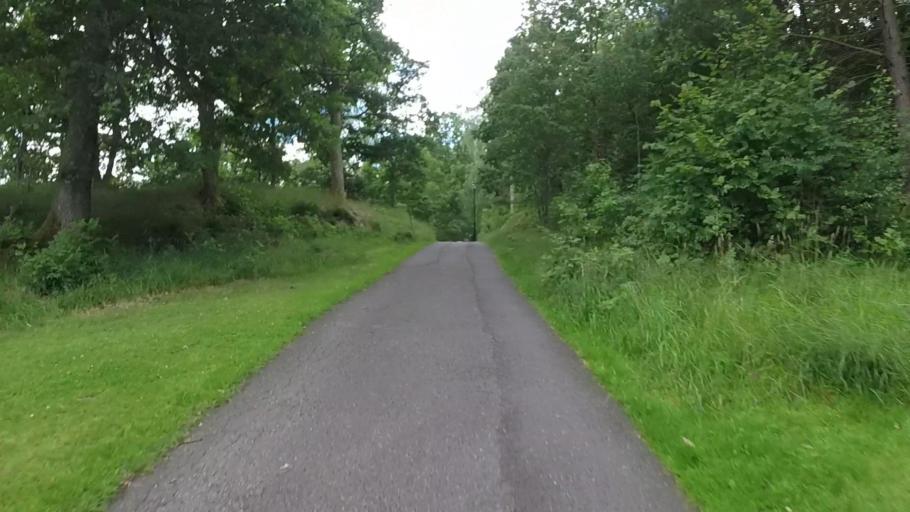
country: SE
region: Vaestra Goetaland
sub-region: Trollhattan
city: Trollhattan
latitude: 58.2842
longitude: 12.2780
